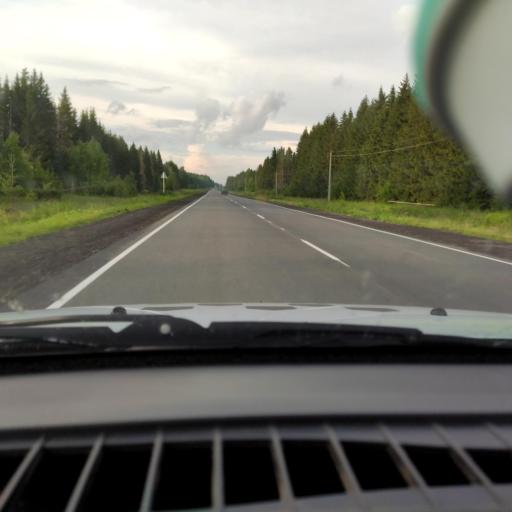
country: RU
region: Perm
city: Orda
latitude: 57.2166
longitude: 56.9438
